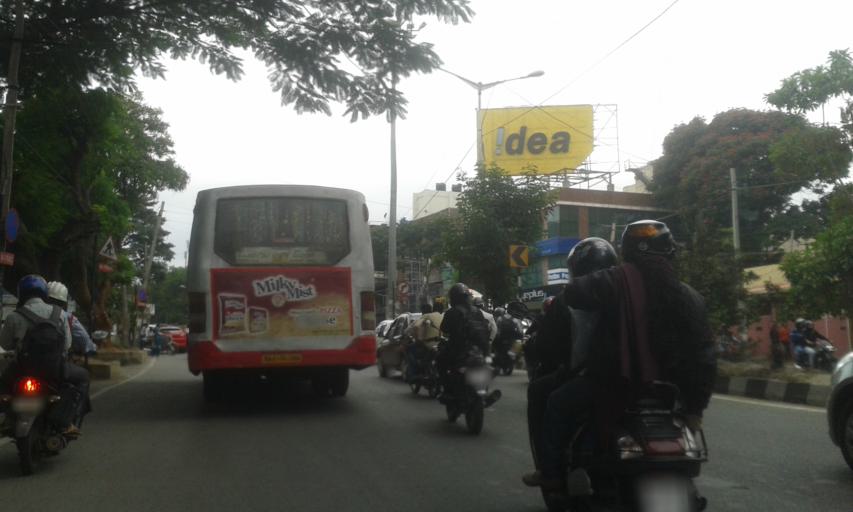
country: IN
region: Karnataka
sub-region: Bangalore Urban
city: Bangalore
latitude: 12.9349
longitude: 77.6242
